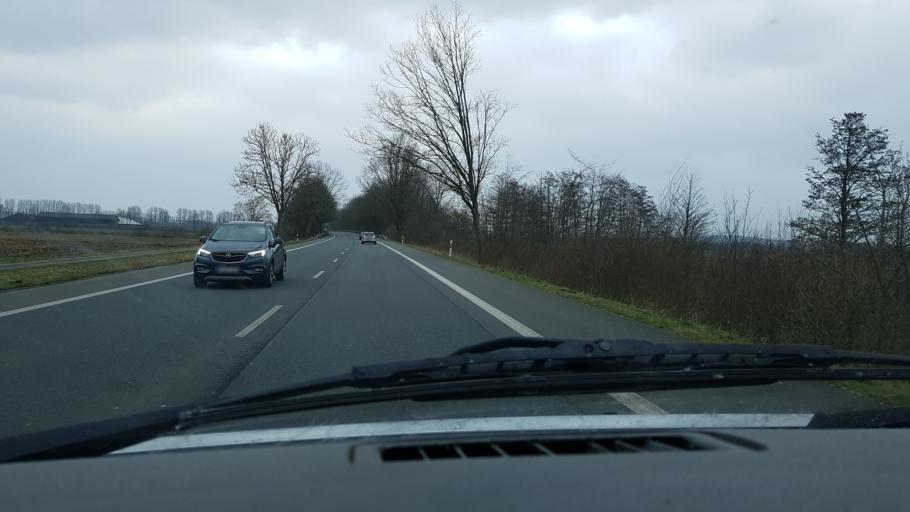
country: NL
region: Gelderland
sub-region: Gemeente Groesbeek
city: De Horst
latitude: 51.8067
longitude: 5.9744
